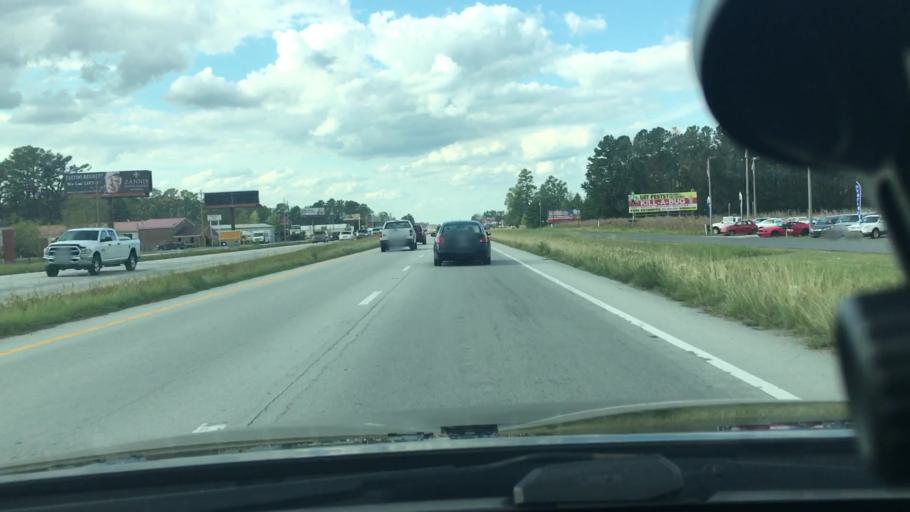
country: US
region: North Carolina
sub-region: Craven County
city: James City
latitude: 35.0568
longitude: -77.0181
